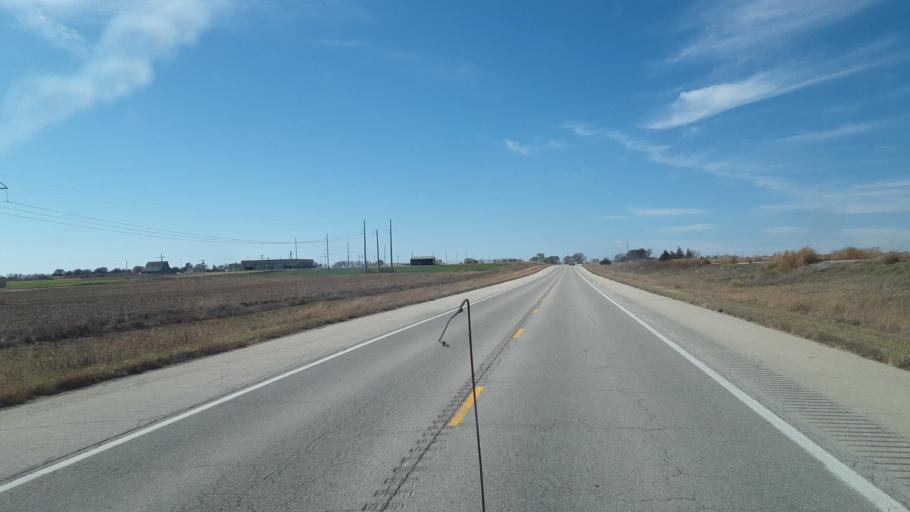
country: US
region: Kansas
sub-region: McPherson County
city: McPherson
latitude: 38.3639
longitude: -97.7645
